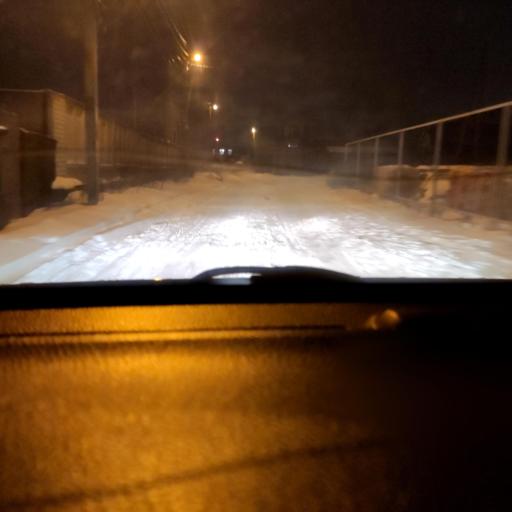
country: RU
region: Voronezj
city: Somovo
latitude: 51.7453
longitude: 39.3316
